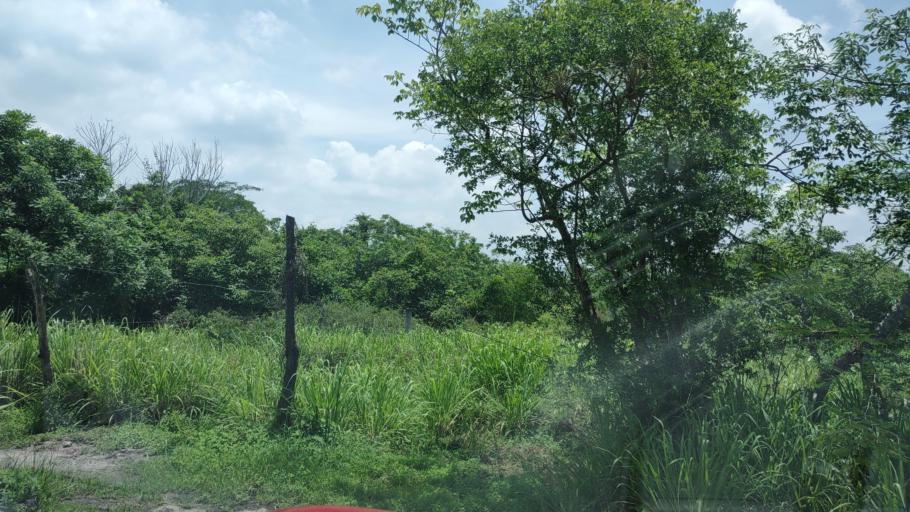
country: MX
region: Veracruz
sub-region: Emiliano Zapata
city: Dos Rios
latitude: 19.4293
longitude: -96.8053
